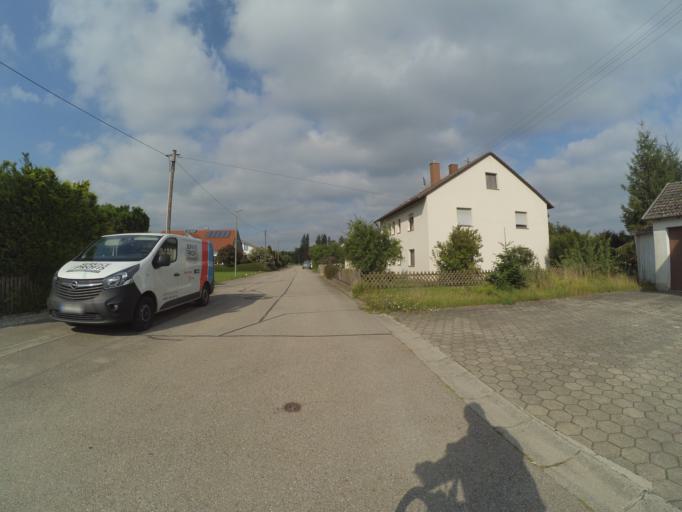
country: DE
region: Bavaria
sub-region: Swabia
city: Waal
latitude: 48.0497
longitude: 10.7852
